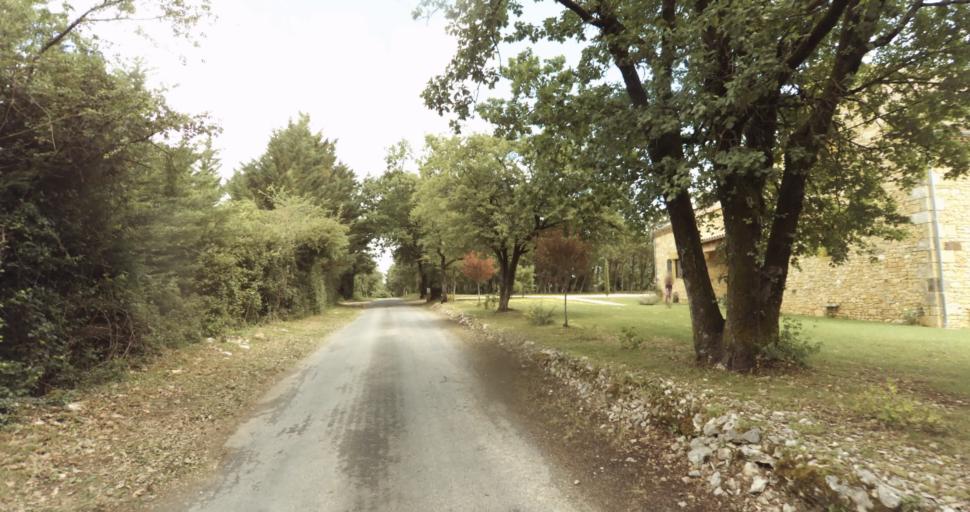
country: FR
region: Aquitaine
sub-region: Departement de la Dordogne
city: Beaumont-du-Perigord
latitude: 44.7559
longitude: 0.7693
